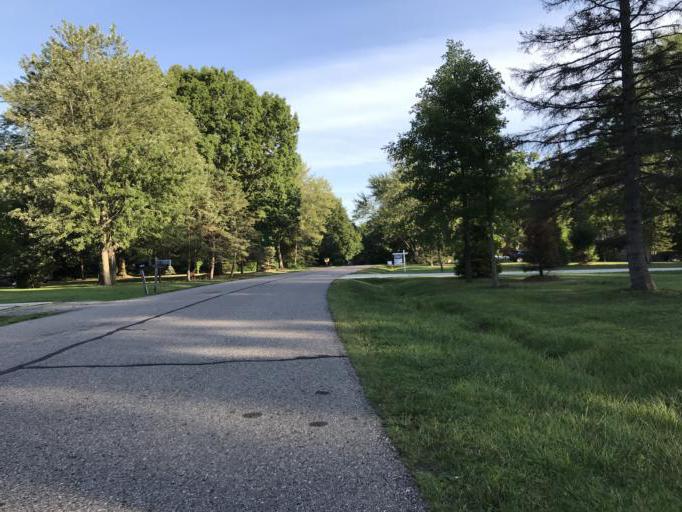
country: US
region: Michigan
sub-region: Oakland County
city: Farmington Hills
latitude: 42.4810
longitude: -83.3463
